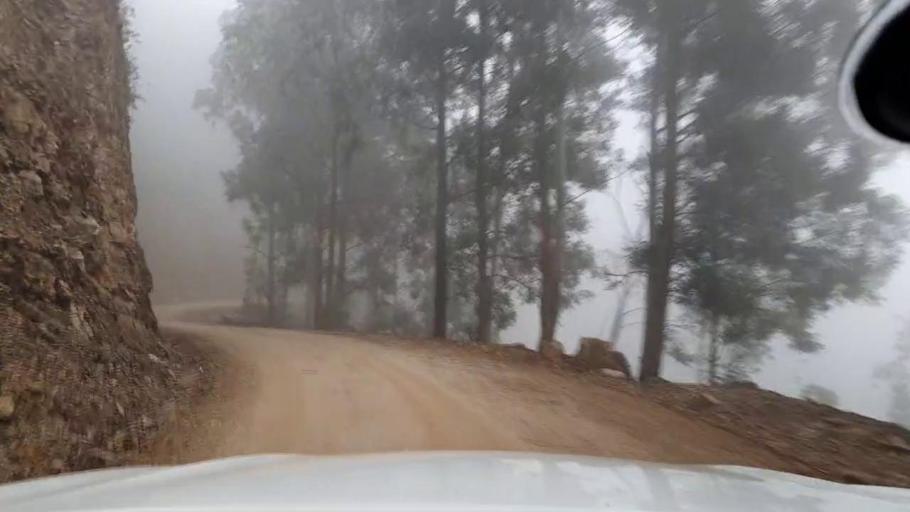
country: RW
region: Western Province
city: Cyangugu
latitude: -2.5902
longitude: 29.1901
